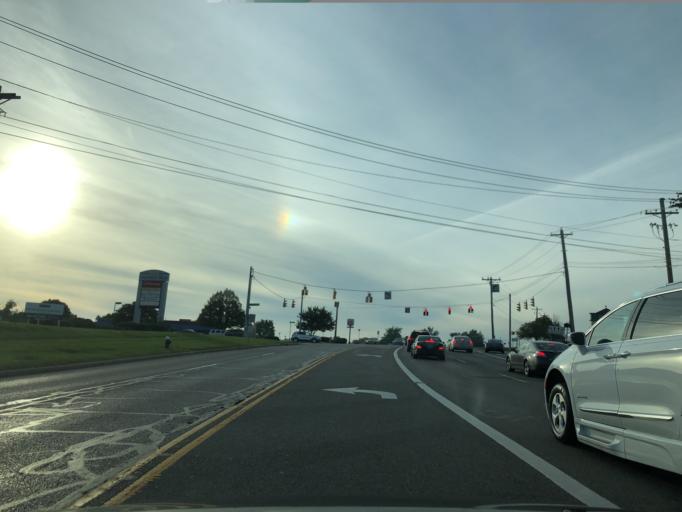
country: US
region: Ohio
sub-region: Warren County
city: Landen
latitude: 39.2910
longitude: -84.3038
